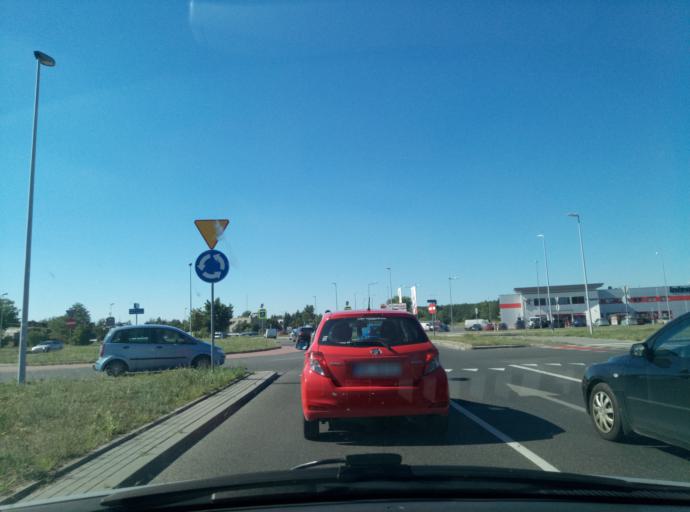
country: PL
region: Kujawsko-Pomorskie
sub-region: Torun
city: Torun
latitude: 53.0406
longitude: 18.5986
